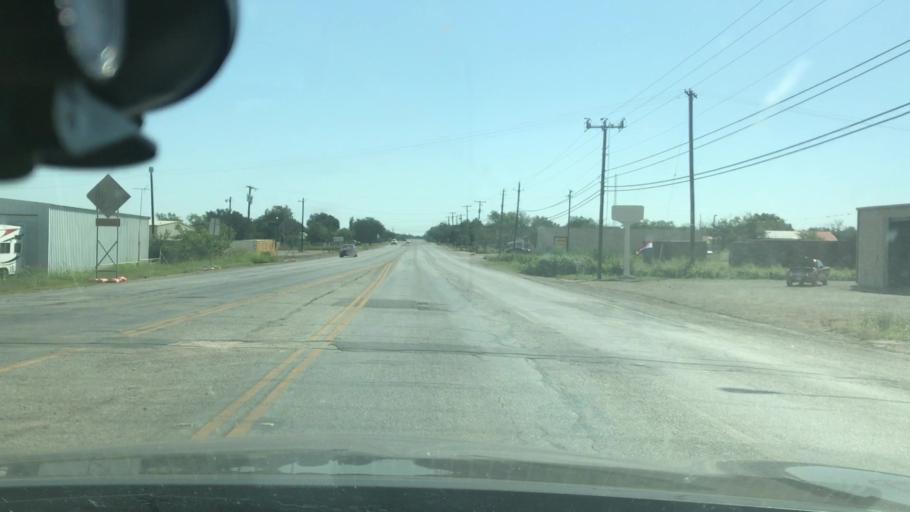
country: US
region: Texas
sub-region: Stephens County
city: Breckenridge
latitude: 32.7554
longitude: -98.8828
